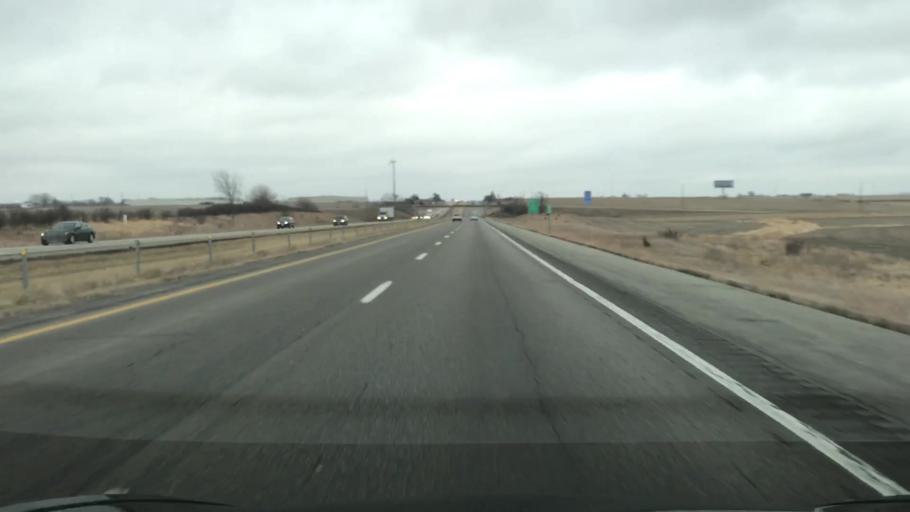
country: US
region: Iowa
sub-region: Guthrie County
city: Stuart
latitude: 41.4929
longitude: -94.3436
